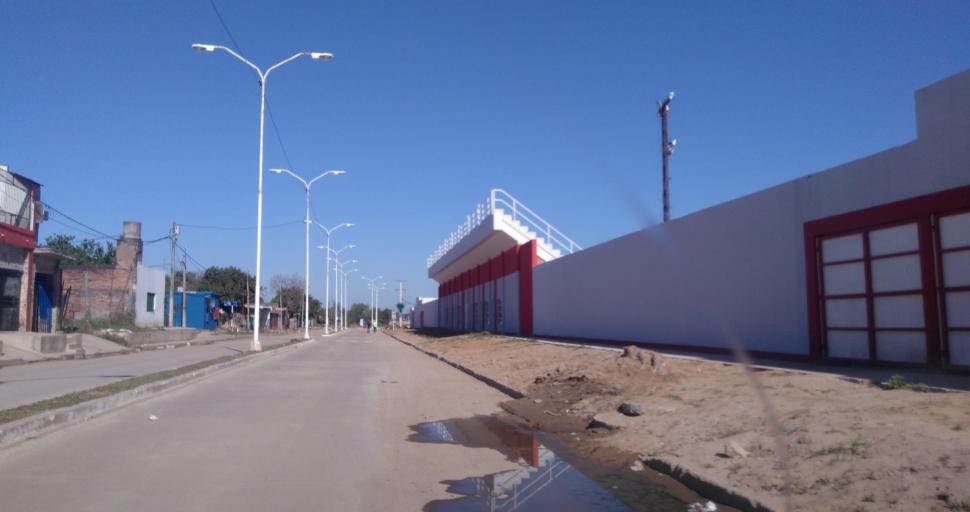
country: AR
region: Chaco
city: Resistencia
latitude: -27.4545
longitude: -58.9684
